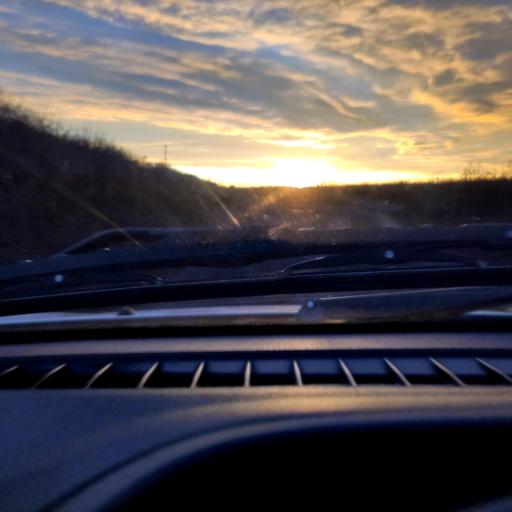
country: RU
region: Samara
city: Tol'yatti
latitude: 53.5972
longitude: 49.4653
